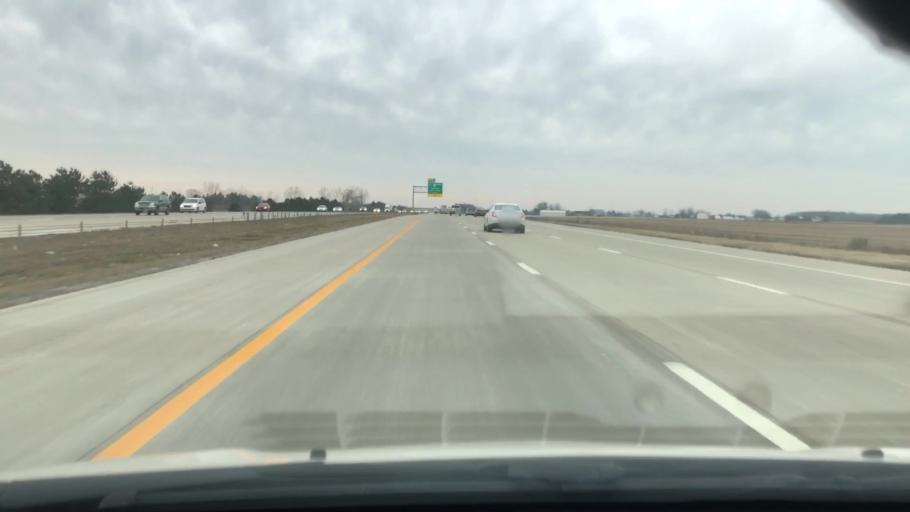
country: US
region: Ohio
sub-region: Wood County
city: Perrysburg
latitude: 41.4946
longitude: -83.6207
